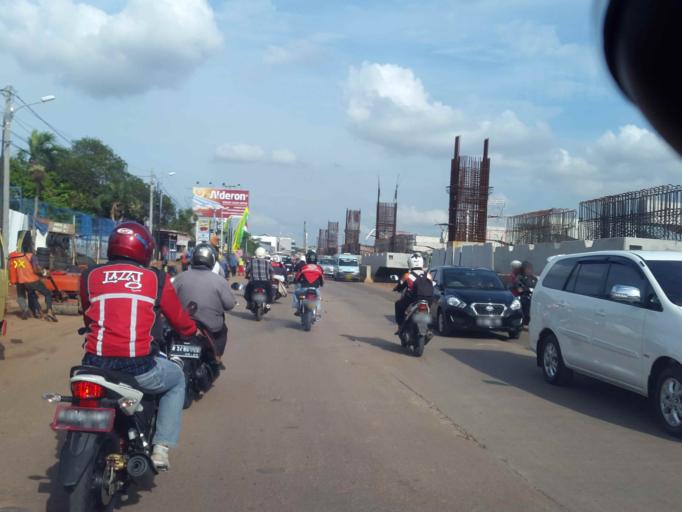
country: ID
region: West Java
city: Bekasi
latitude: -6.2478
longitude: 106.9182
